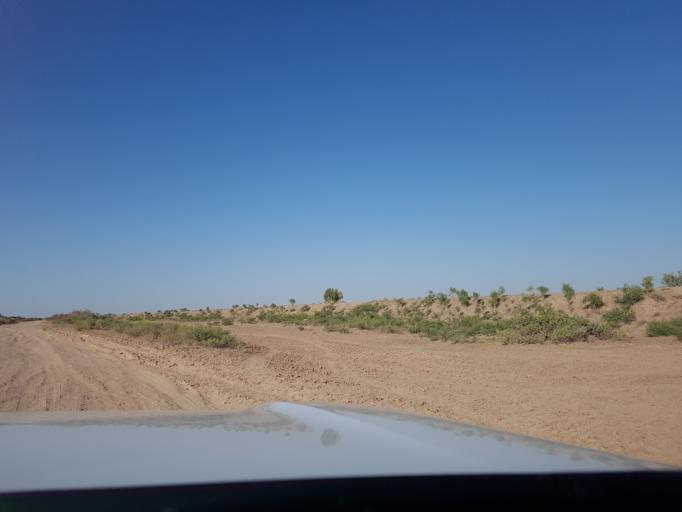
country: IR
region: Razavi Khorasan
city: Sarakhs
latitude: 36.9756
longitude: 61.3848
